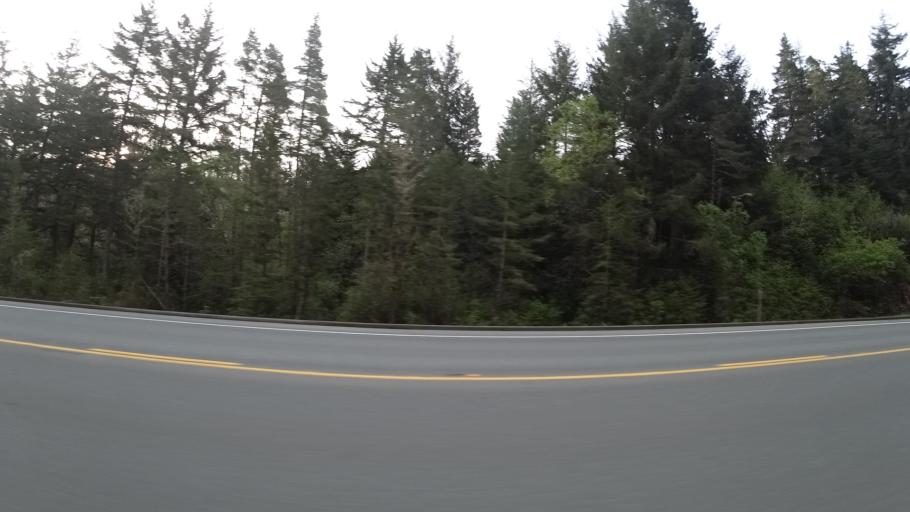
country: US
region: Oregon
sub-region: Coos County
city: Lakeside
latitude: 43.5706
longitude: -124.1991
